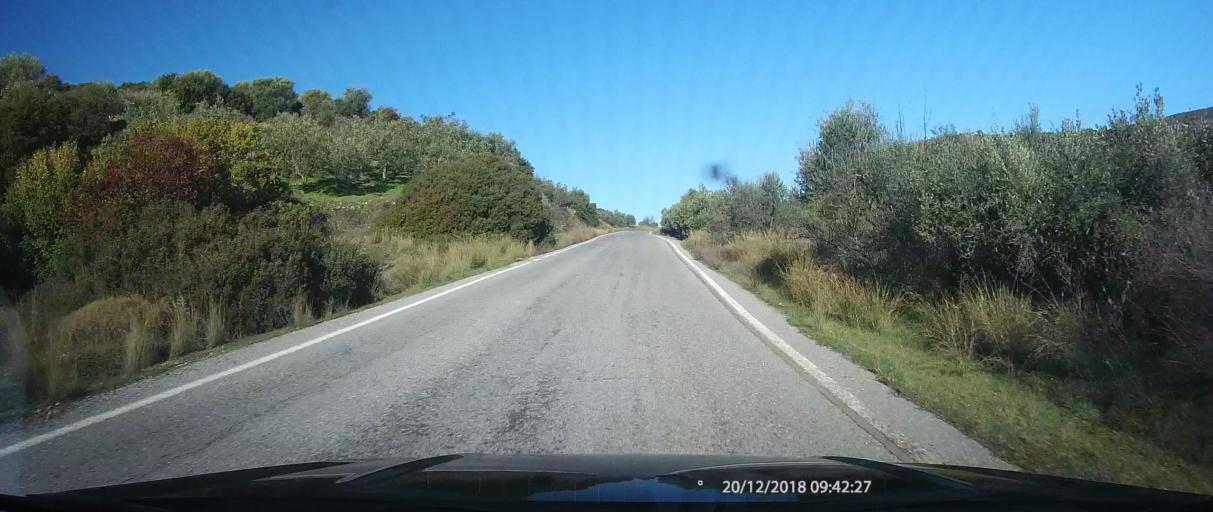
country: GR
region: Peloponnese
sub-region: Nomos Lakonias
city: Yerakion
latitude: 36.9600
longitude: 22.7541
